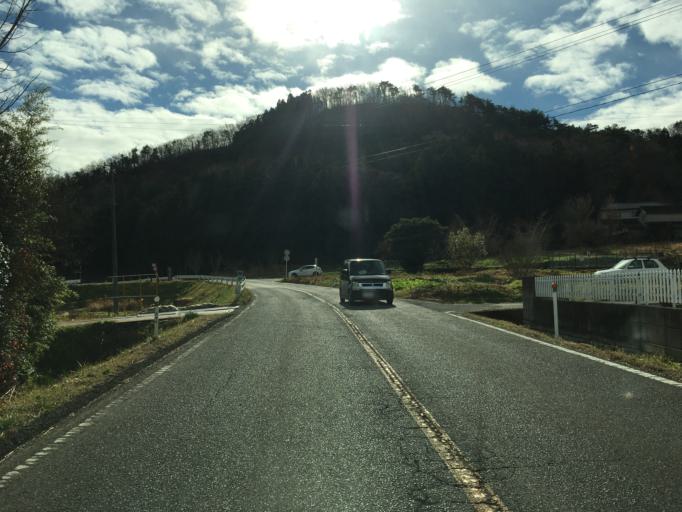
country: JP
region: Fukushima
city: Motomiya
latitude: 37.5187
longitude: 140.3694
